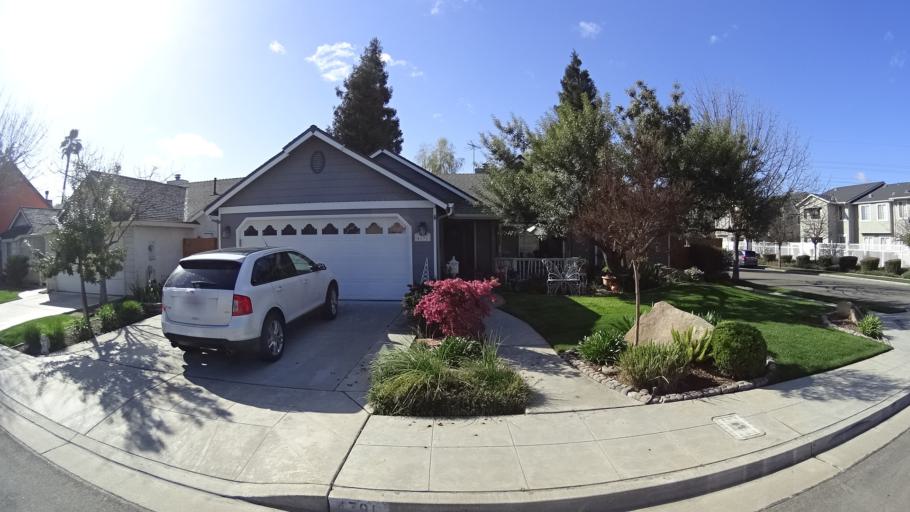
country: US
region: California
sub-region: Fresno County
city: West Park
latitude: 36.8231
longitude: -119.8806
